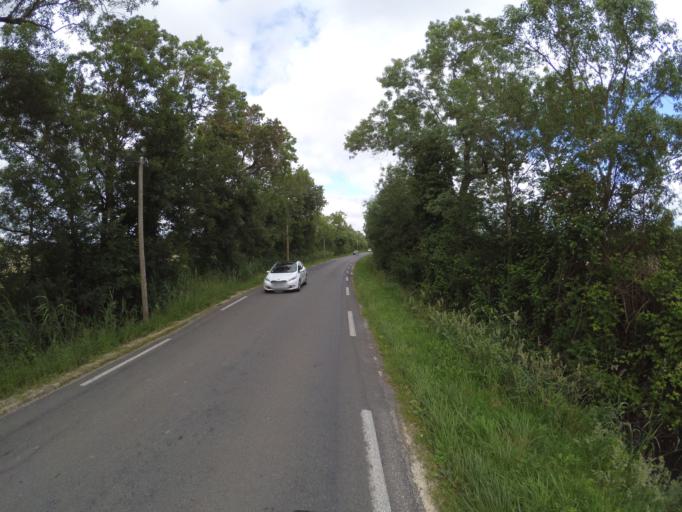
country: FR
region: Aquitaine
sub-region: Departement de la Gironde
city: Ludon-Medoc
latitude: 44.9850
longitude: -0.5733
